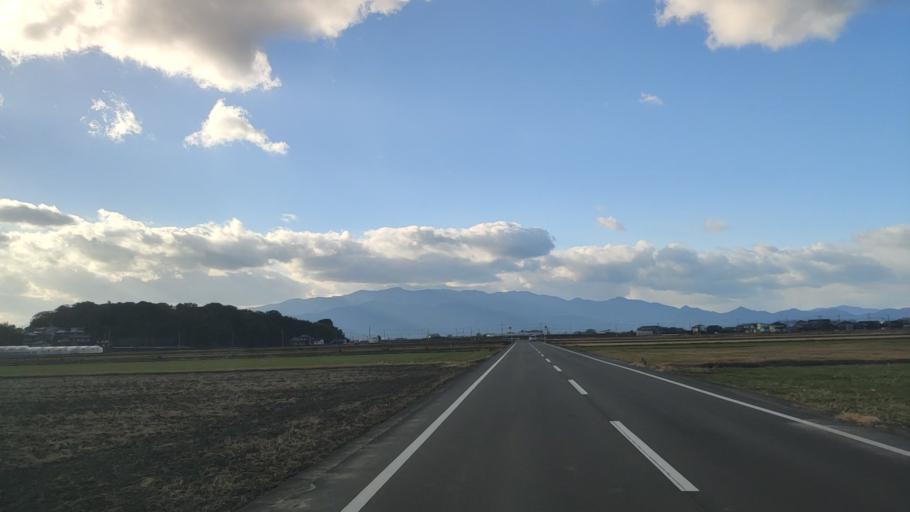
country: JP
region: Ehime
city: Saijo
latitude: 33.9034
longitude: 133.1354
